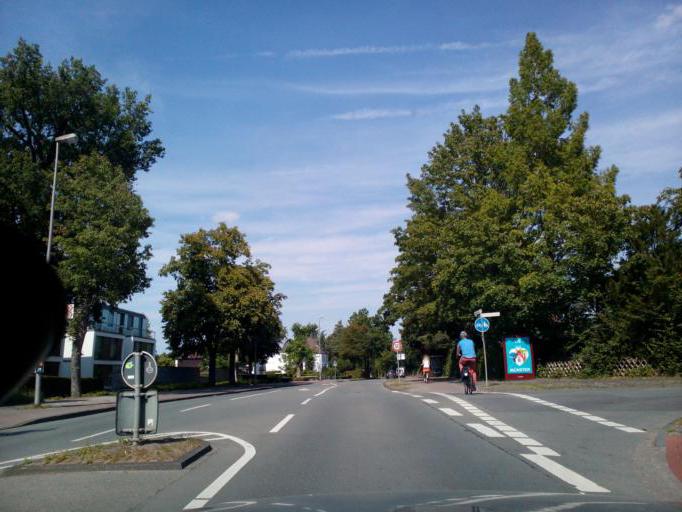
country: DE
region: North Rhine-Westphalia
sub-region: Regierungsbezirk Munster
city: Muenster
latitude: 51.9445
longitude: 7.6010
